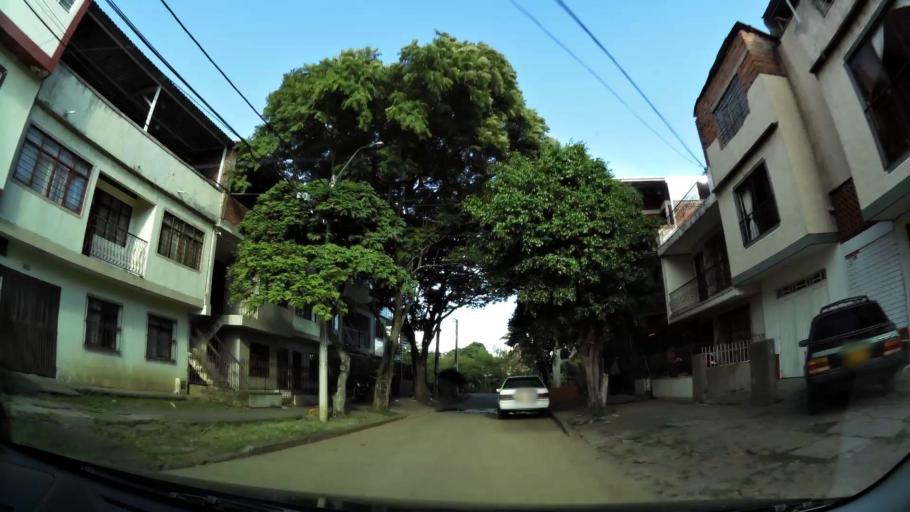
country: CO
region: Valle del Cauca
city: Cali
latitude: 3.4315
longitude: -76.5205
